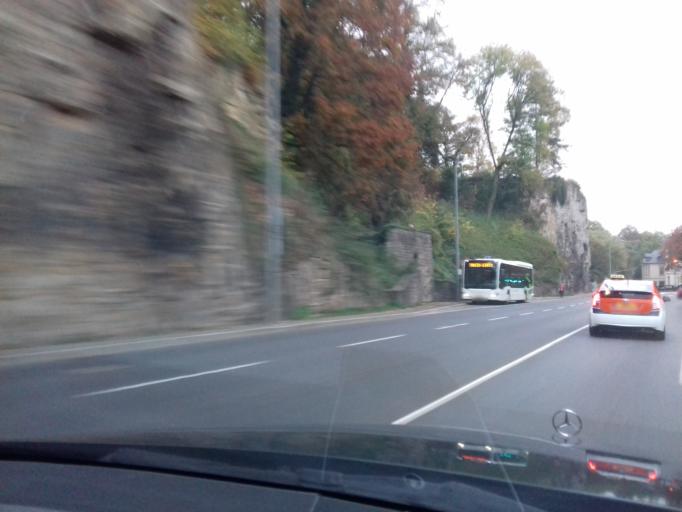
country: LU
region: Luxembourg
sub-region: Canton de Luxembourg
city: Luxembourg
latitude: 49.6185
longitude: 6.1302
